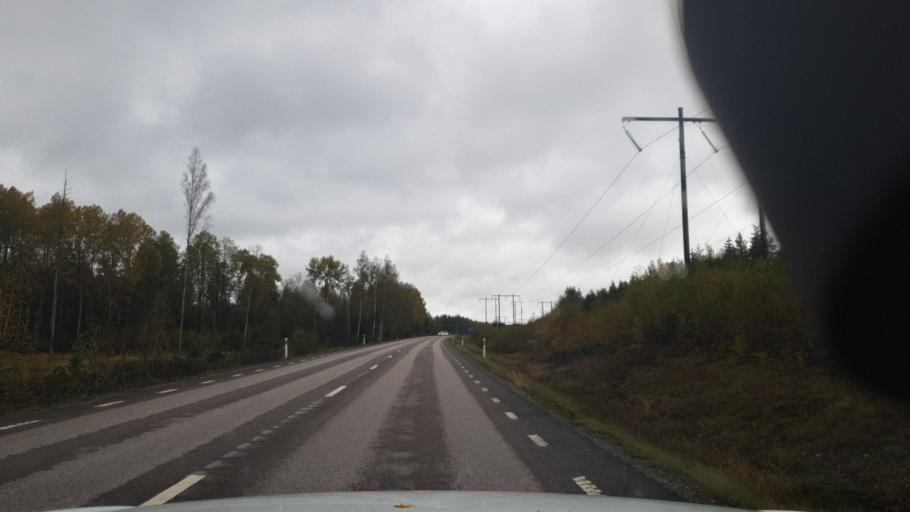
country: SE
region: Vaermland
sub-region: Karlstads Kommun
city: Valberg
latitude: 59.4112
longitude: 13.1836
